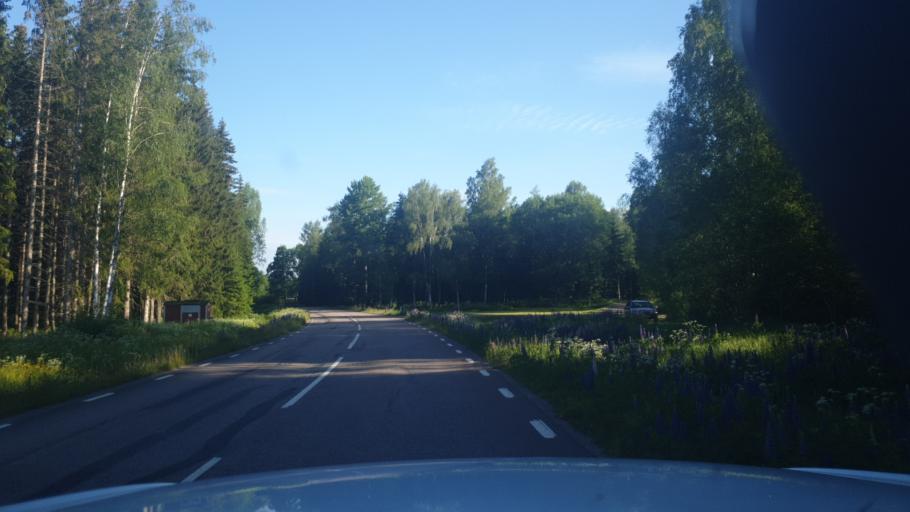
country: SE
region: Vaermland
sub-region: Eda Kommun
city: Charlottenberg
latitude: 59.9022
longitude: 12.3002
